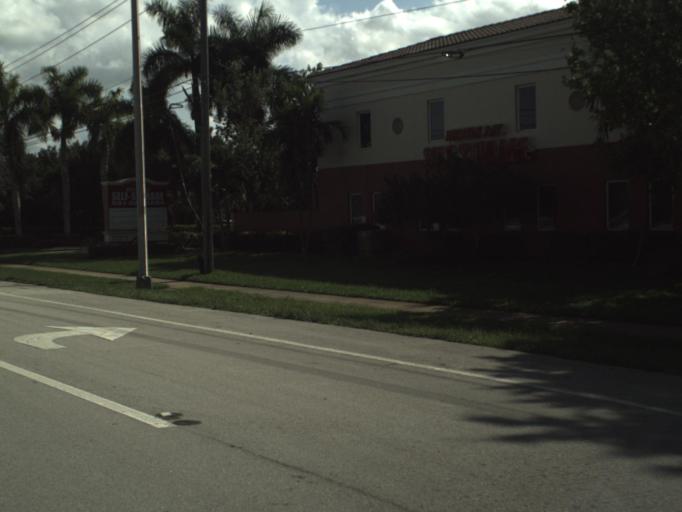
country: US
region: Florida
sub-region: Palm Beach County
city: Boca Pointe
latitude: 26.3745
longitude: -80.2037
